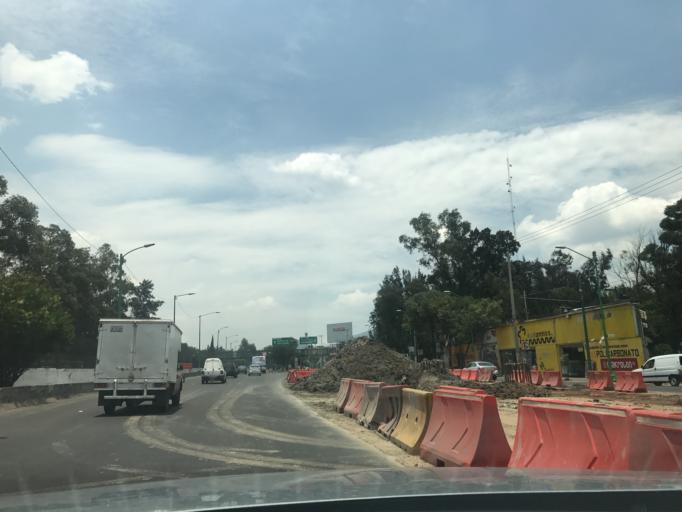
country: MX
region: Mexico
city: Colonia Lindavista
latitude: 19.4945
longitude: -99.1465
